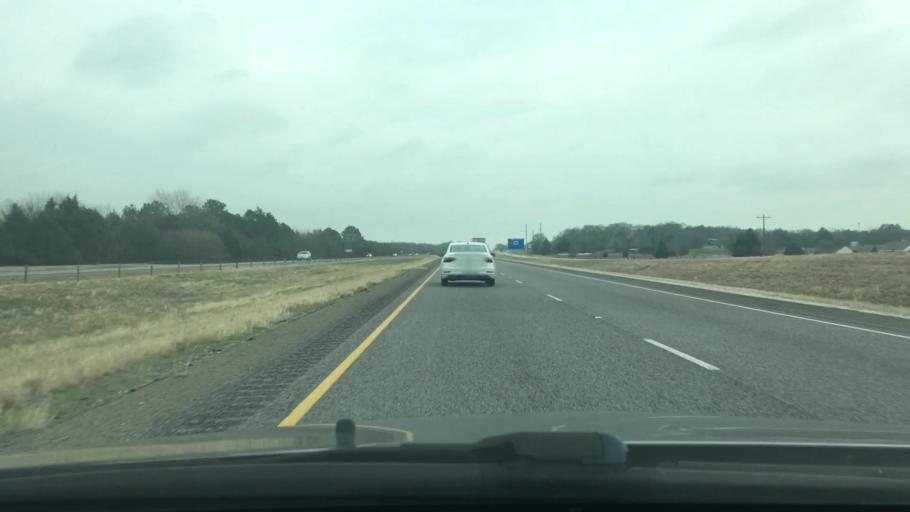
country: US
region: Texas
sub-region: Freestone County
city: Fairfield
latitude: 31.7395
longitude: -96.1896
